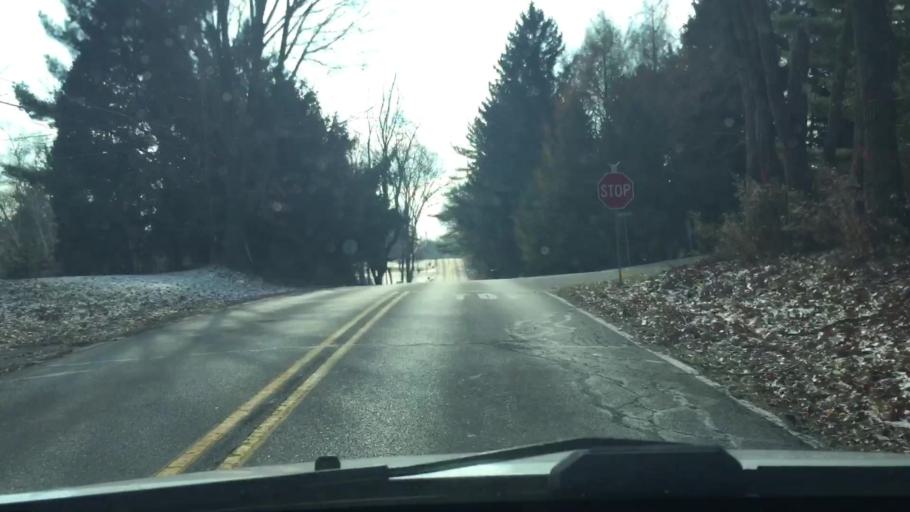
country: US
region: Wisconsin
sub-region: Waukesha County
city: Waukesha
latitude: 42.9803
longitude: -88.2873
